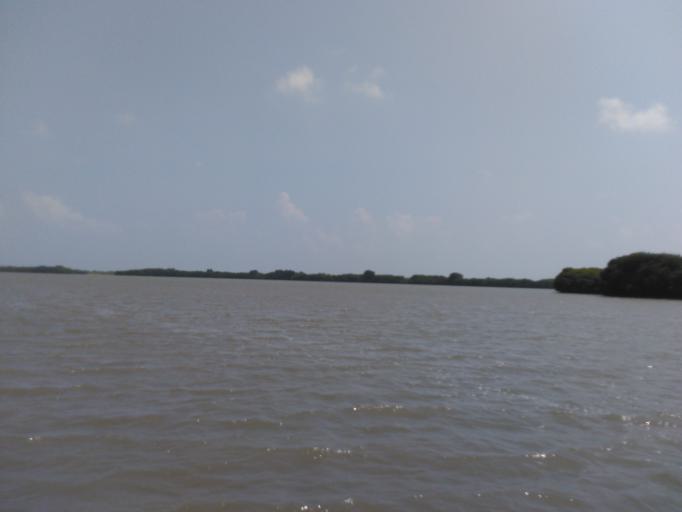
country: IN
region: Tamil Nadu
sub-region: Cuddalore
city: Annamalainagar
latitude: 11.4414
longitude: 79.7913
